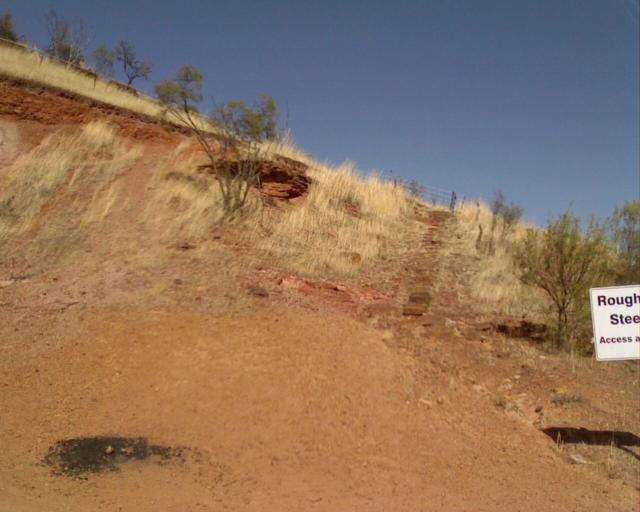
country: AU
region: Western Australia
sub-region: Irwin
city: Dongara
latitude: -29.1860
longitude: 115.4376
